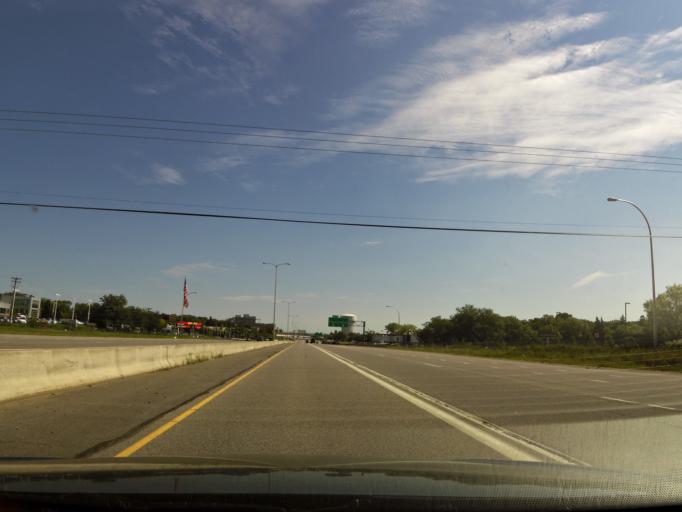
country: US
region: Minnesota
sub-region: Hennepin County
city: Minnetonka Mills
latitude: 44.9710
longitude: -93.4543
